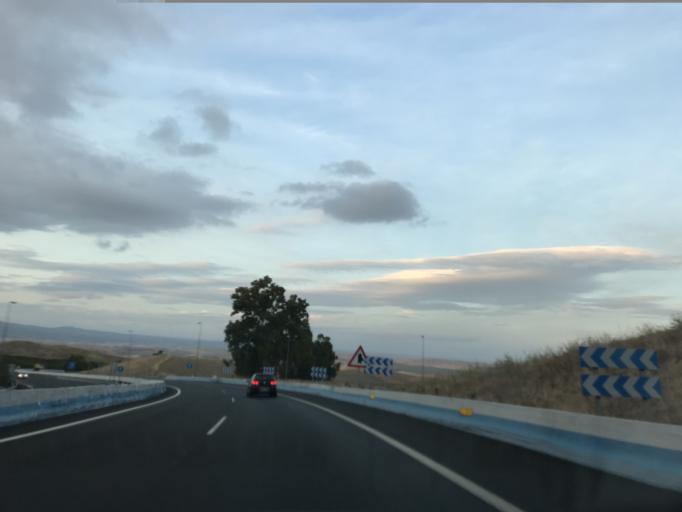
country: ES
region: Andalusia
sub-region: Province of Cordoba
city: La Victoria
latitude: 37.7616
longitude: -4.8231
